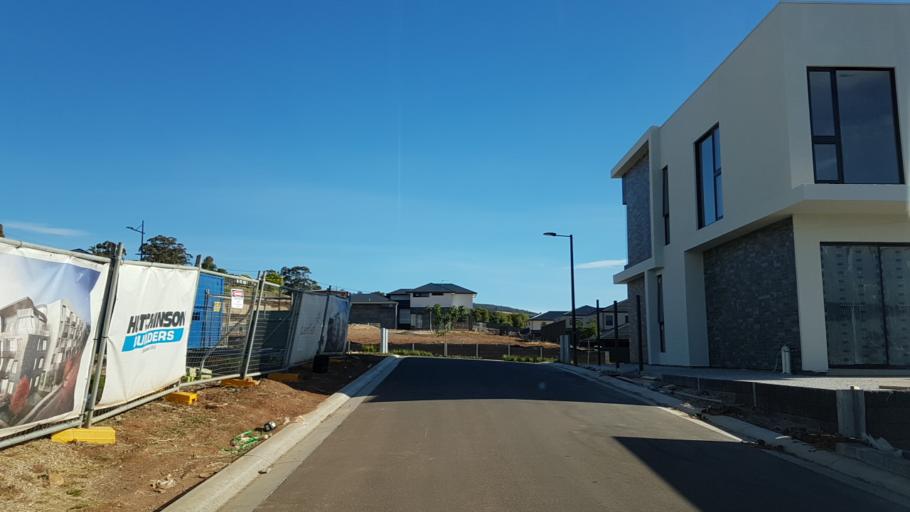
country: AU
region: South Australia
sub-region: Adelaide Hills
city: Adelaide Hills
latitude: -34.9057
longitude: 138.6869
